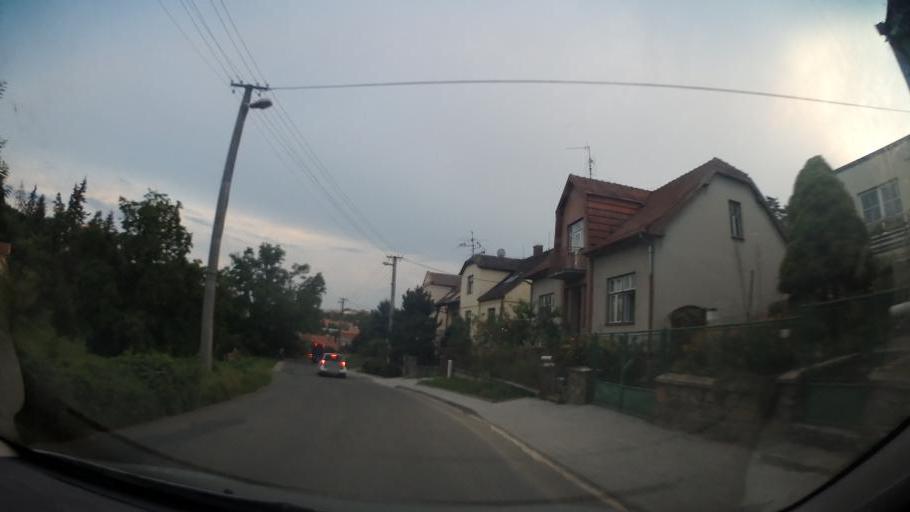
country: CZ
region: South Moravian
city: Dolni Kounice
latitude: 49.0725
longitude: 16.4715
